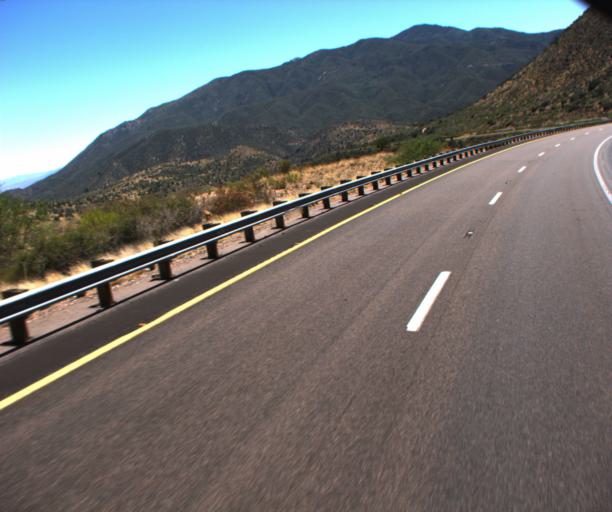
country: US
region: Arizona
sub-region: Gila County
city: Tonto Basin
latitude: 33.9842
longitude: -111.3834
